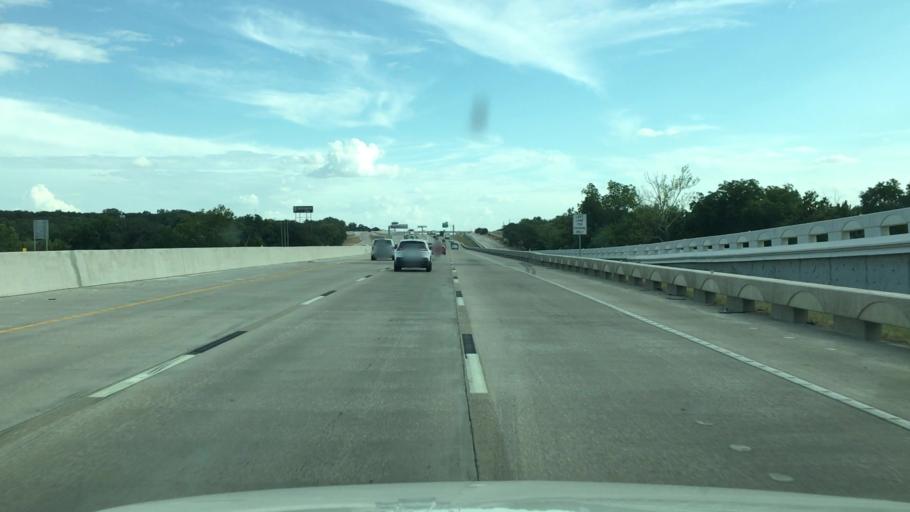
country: US
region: Texas
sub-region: Bell County
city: Salado
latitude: 30.9455
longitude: -97.5394
